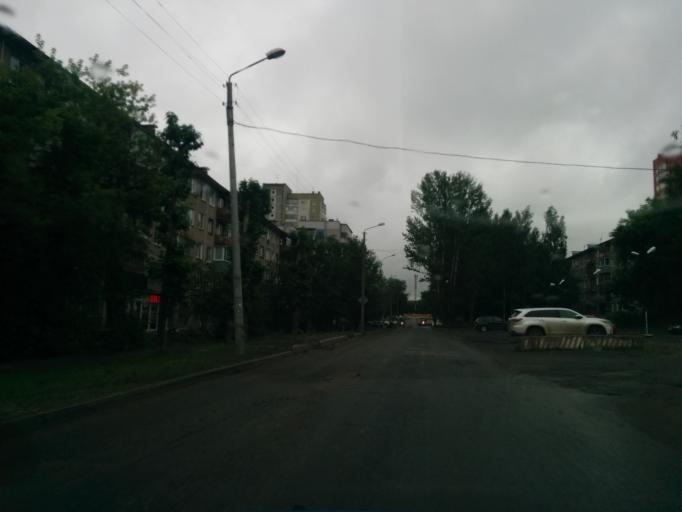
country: RU
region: Perm
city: Perm
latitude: 57.9914
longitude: 56.2320
